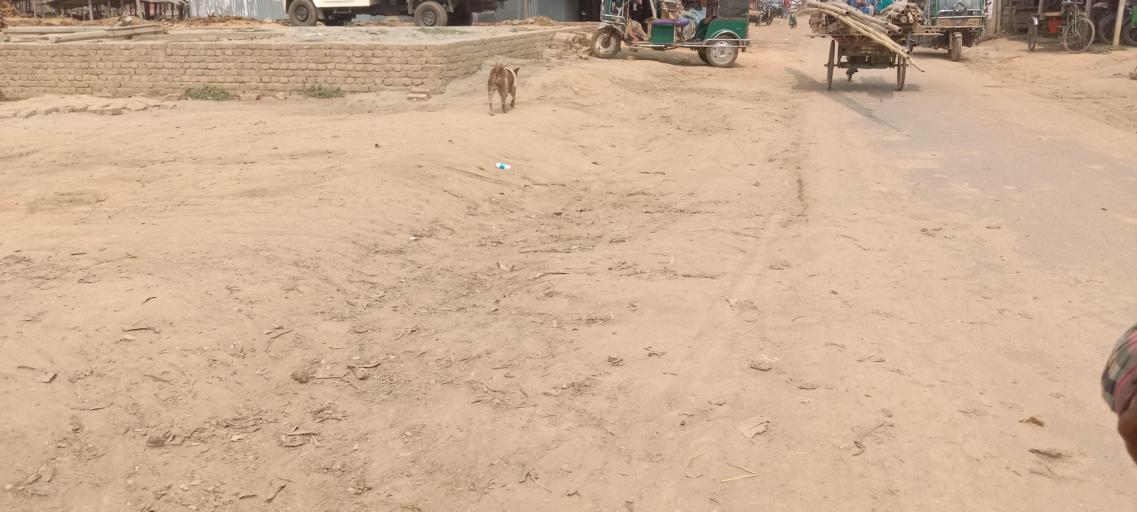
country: BD
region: Dhaka
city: Sakhipur
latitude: 24.3071
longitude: 90.2687
